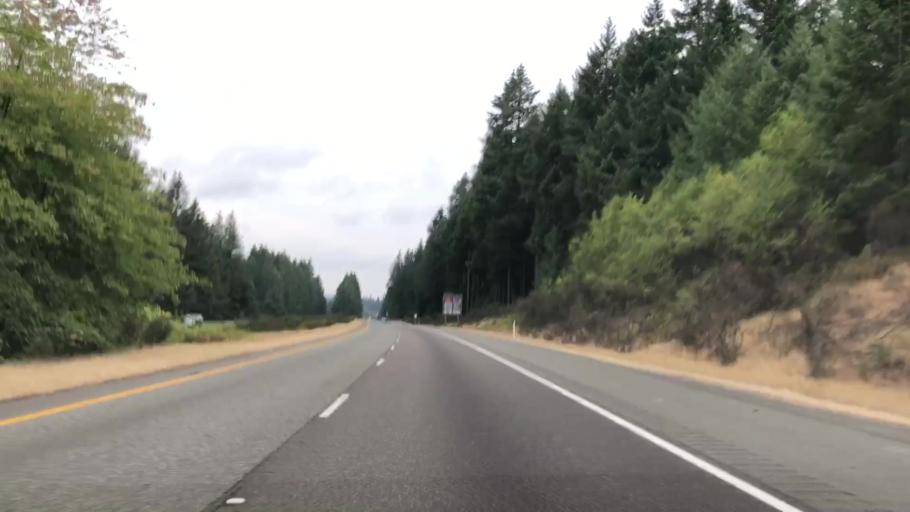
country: US
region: Washington
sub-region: Kitsap County
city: Bethel
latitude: 47.4906
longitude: -122.6352
